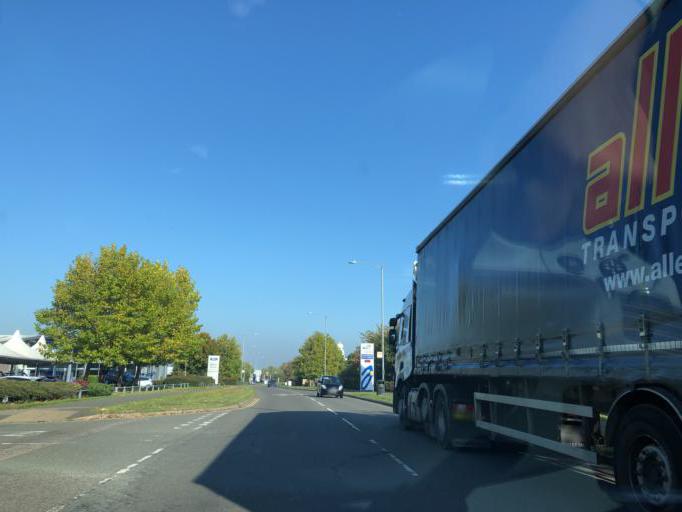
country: GB
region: England
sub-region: Warwickshire
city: Royal Leamington Spa
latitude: 52.2742
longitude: -1.5445
